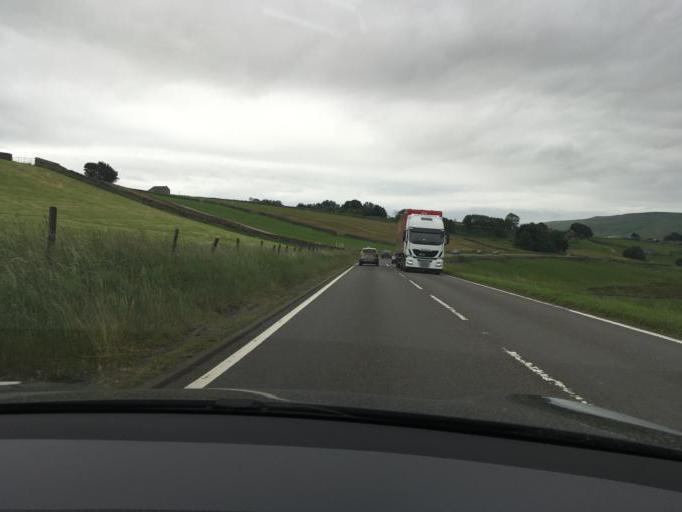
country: GB
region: England
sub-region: Derbyshire
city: Chapel en le Frith
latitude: 53.3190
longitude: -1.8670
